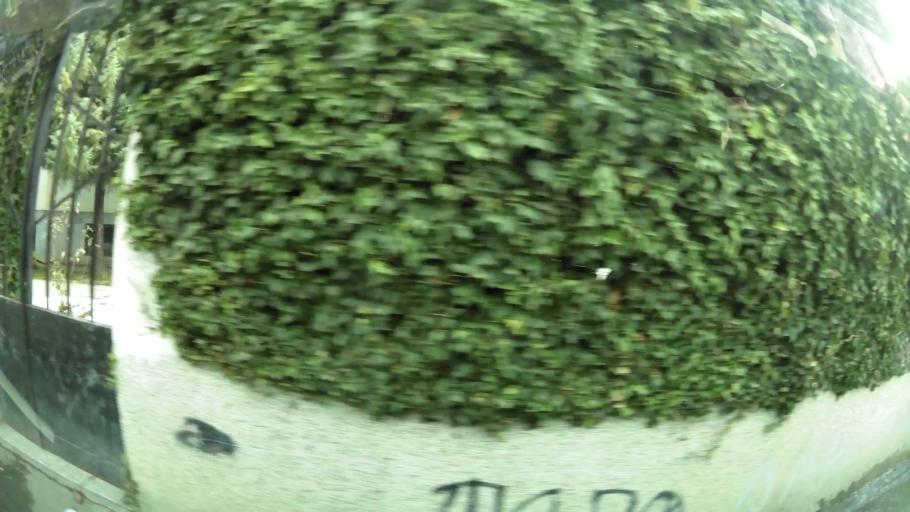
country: MK
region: Cair
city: Cair
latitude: 42.0089
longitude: 21.4454
